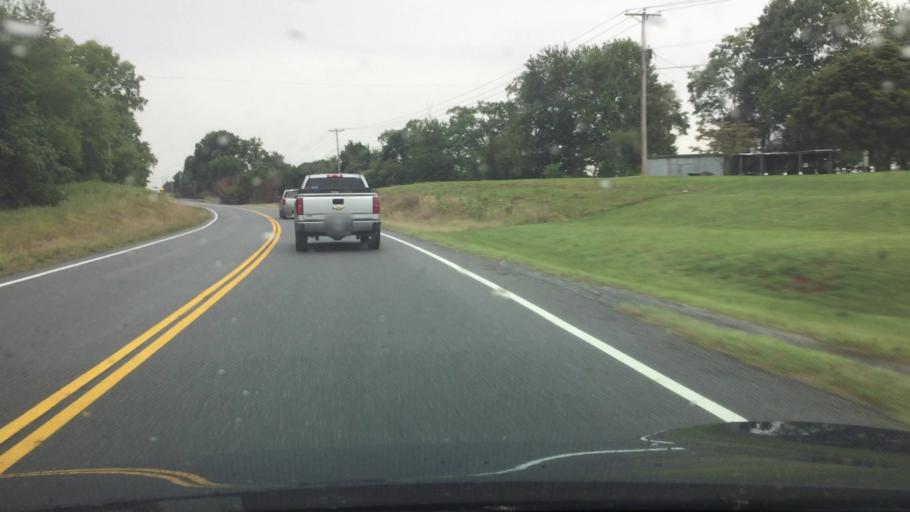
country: US
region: Virginia
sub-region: City of Bedford
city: Bedford
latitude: 37.3625
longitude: -79.4537
